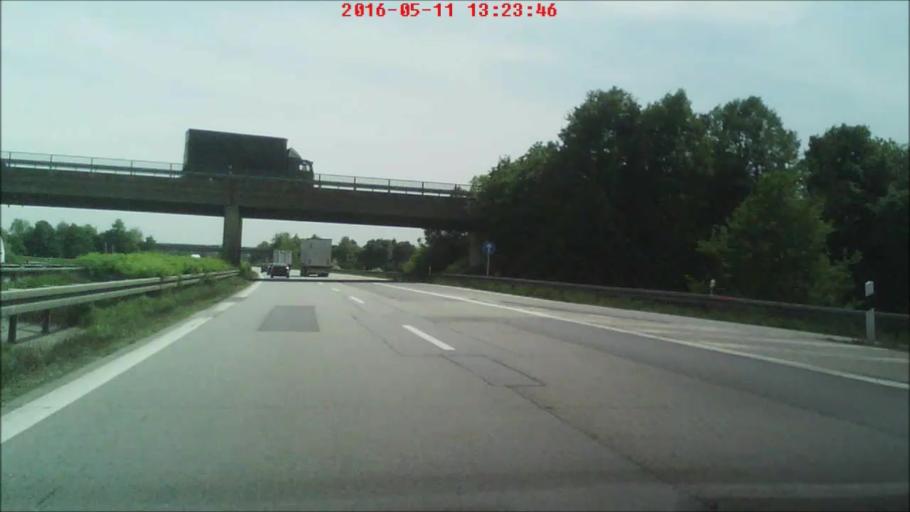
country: AT
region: Upper Austria
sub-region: Politischer Bezirk Scharding
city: Scharding
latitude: 48.4372
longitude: 13.3763
